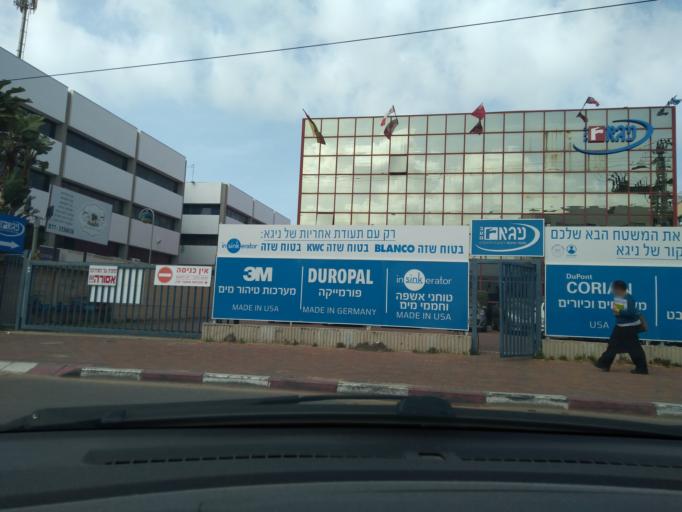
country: IL
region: Central District
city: Even Yehuda
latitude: 32.2782
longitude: 34.8587
